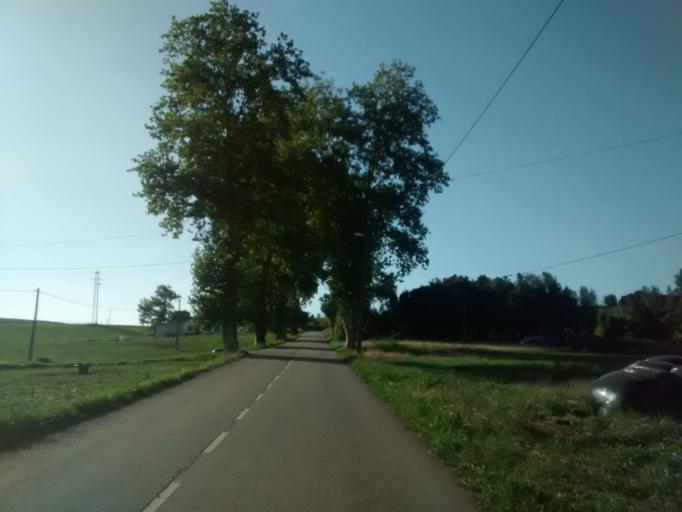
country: ES
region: Cantabria
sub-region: Provincia de Cantabria
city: Lierganes
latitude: 43.4052
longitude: -3.7397
